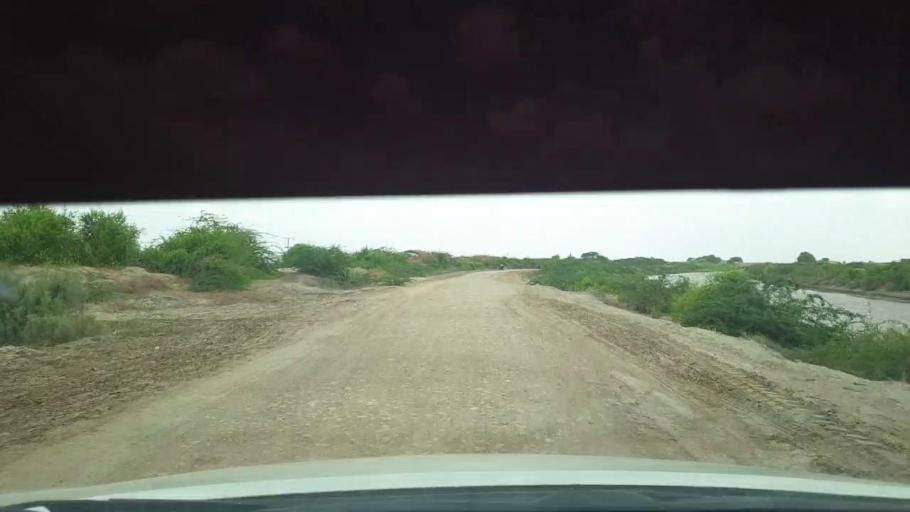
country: PK
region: Sindh
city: Kadhan
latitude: 24.4695
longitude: 69.0511
